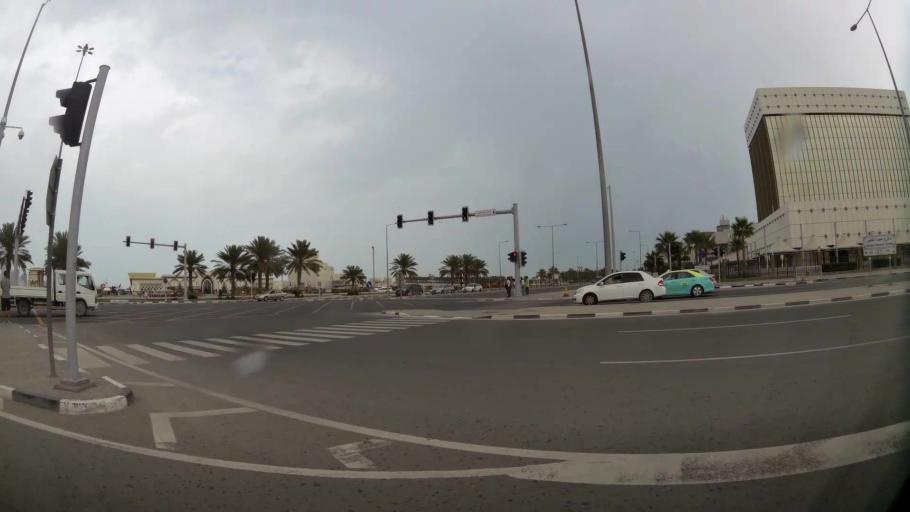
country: QA
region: Baladiyat ad Dawhah
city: Doha
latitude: 25.2907
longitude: 51.5344
